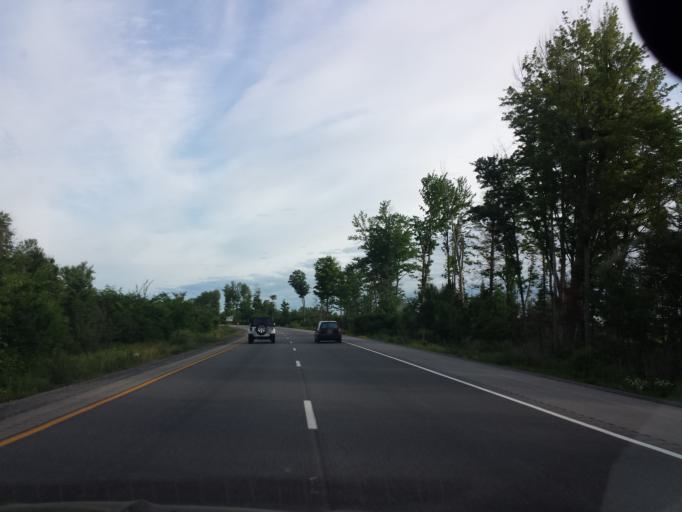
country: CA
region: Ontario
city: Arnprior
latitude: 45.4142
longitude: -76.3016
